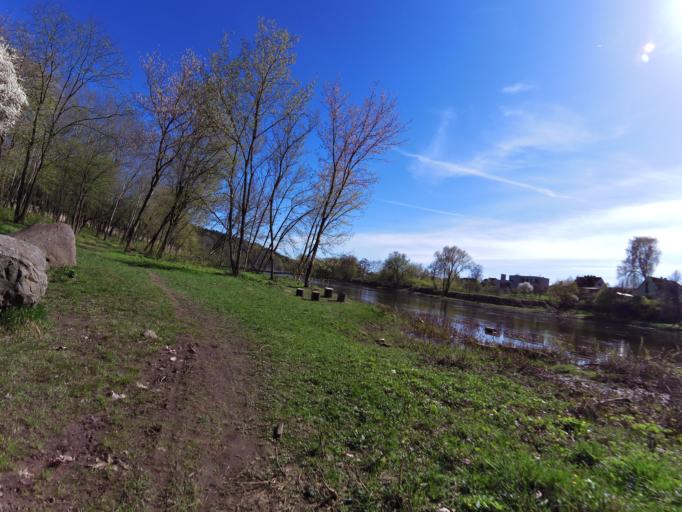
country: LT
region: Vilnius County
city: Vilkpede
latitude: 54.6838
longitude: 25.2288
